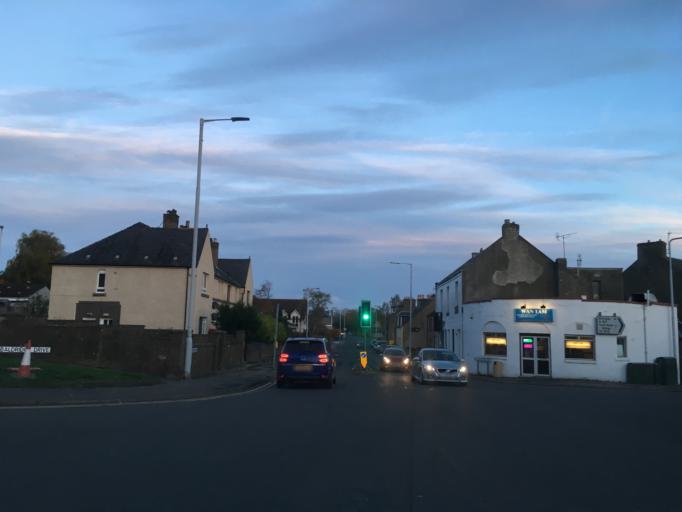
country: GB
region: Scotland
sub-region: Fife
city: Dunfermline
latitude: 56.0774
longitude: -3.4781
